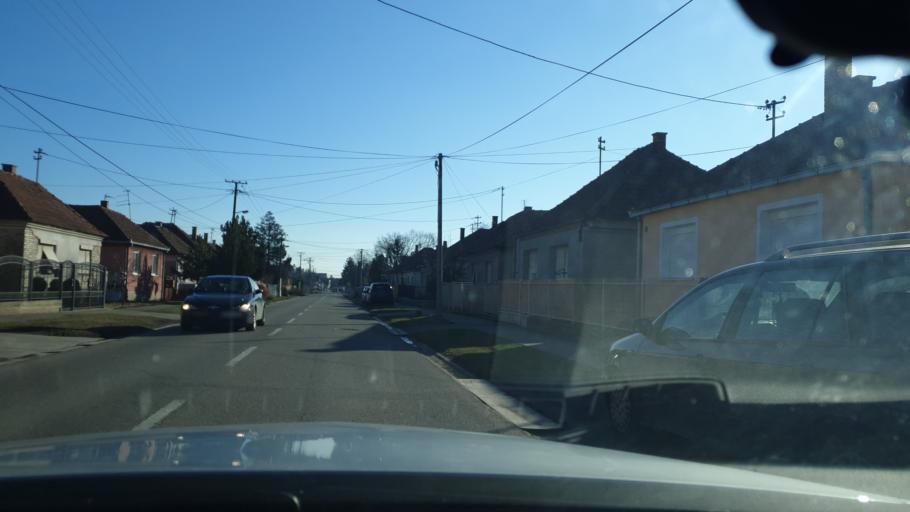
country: RS
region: Autonomna Pokrajina Vojvodina
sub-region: Sremski Okrug
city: Ruma
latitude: 45.0179
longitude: 19.8167
